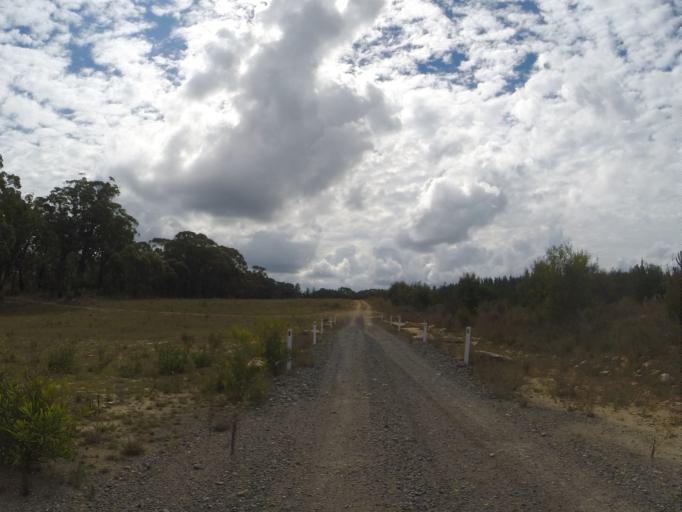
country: AU
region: New South Wales
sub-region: Wingecarribee
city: Moss Vale
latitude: -34.5226
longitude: 150.2250
